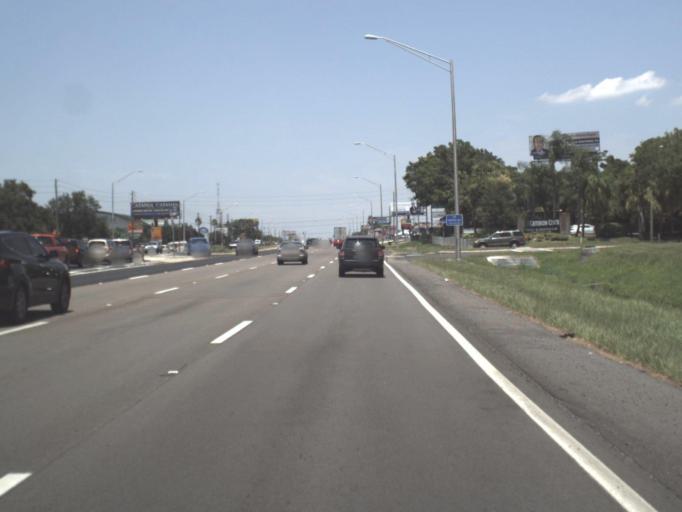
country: US
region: Florida
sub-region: Pinellas County
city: Saint George
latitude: 28.0398
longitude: -82.7381
